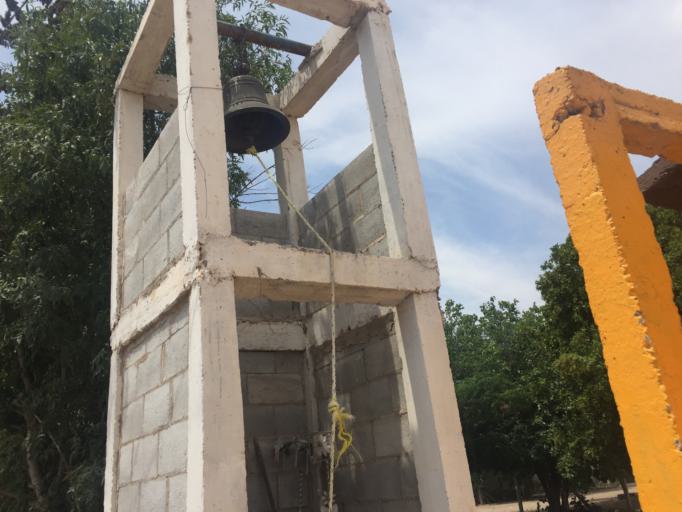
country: MX
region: Durango
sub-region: Gomez Palacio
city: San Jose de Vinedo
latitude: 25.6674
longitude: -103.4240
